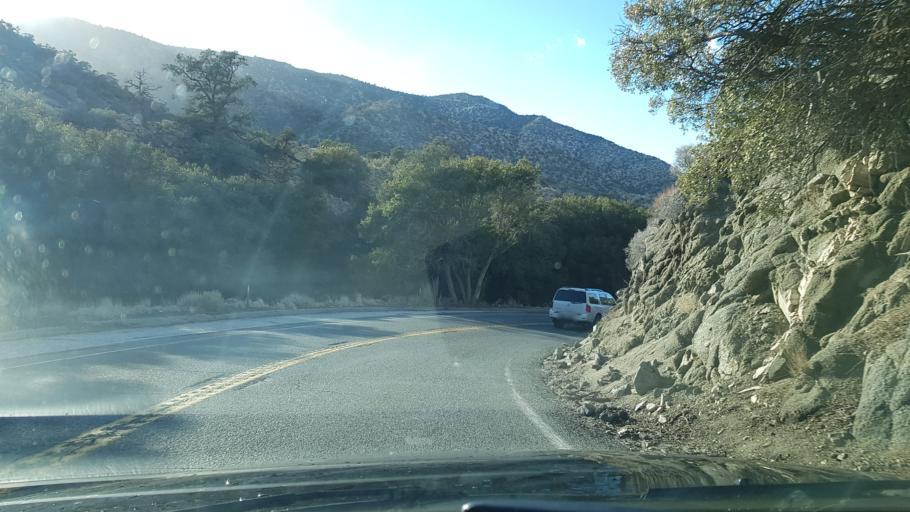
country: US
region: California
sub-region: San Bernardino County
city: Big Bear City
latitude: 34.3334
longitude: -116.8299
